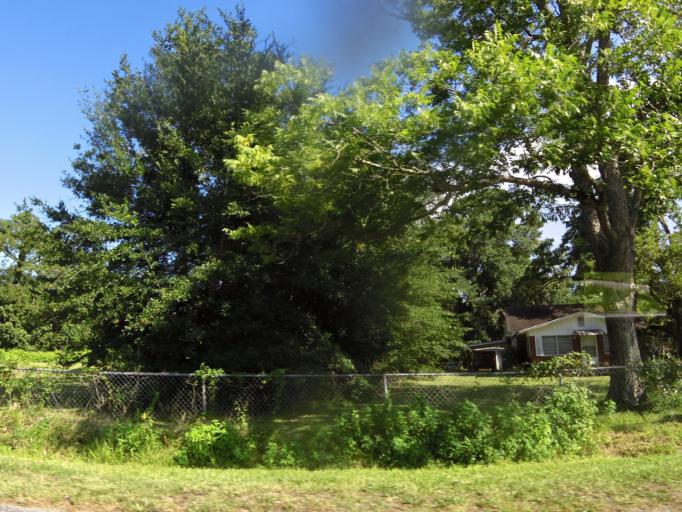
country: US
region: Florida
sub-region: Nassau County
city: Fernandina Beach
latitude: 30.6371
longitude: -81.4625
